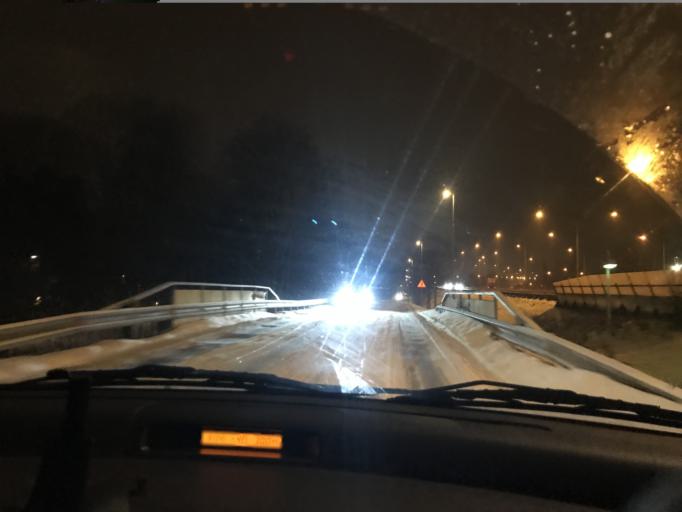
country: SE
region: Stockholm
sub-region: Nacka Kommun
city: Fisksatra
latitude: 59.3135
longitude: 18.2343
